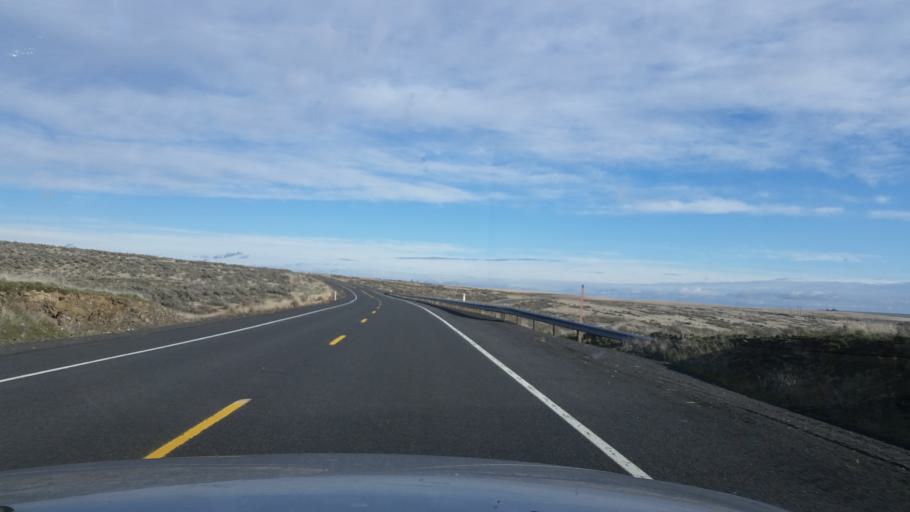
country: US
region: Washington
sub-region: Adams County
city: Ritzville
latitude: 47.3675
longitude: -118.4566
